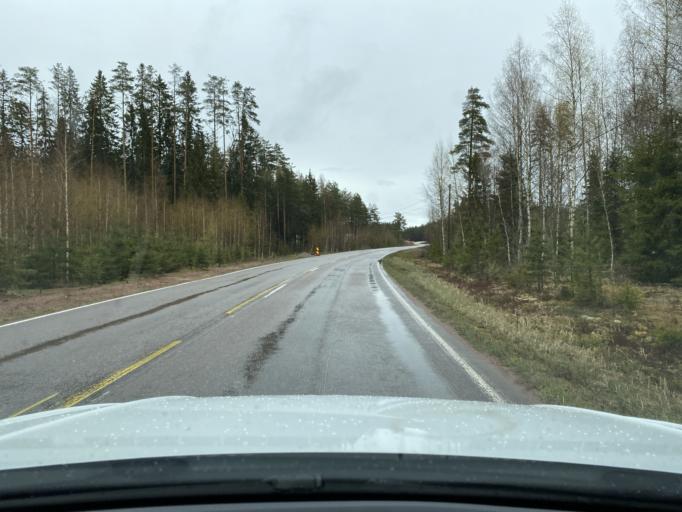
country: FI
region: Satakunta
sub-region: Pori
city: Vampula
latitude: 60.9562
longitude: 22.6670
